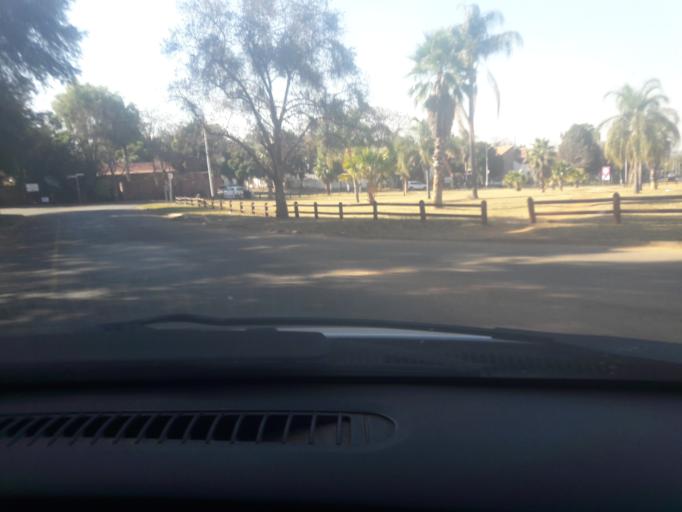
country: ZA
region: Gauteng
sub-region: City of Tshwane Metropolitan Municipality
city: Pretoria
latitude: -25.7690
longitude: 28.2645
